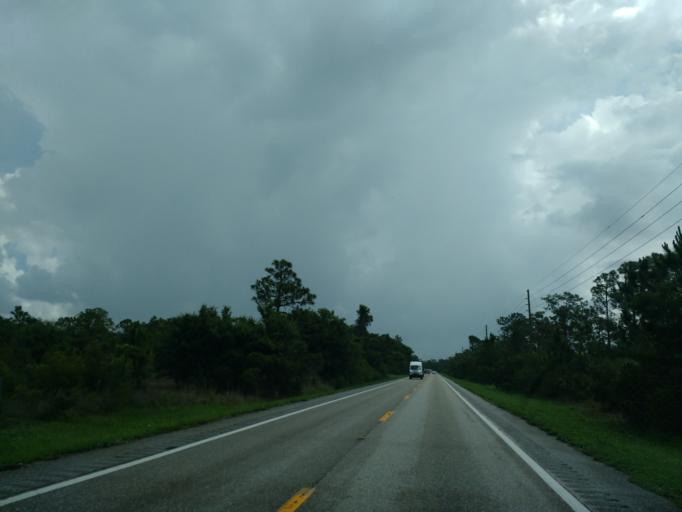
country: US
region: Florida
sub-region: Lee County
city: Burnt Store Marina
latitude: 26.8091
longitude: -82.0274
